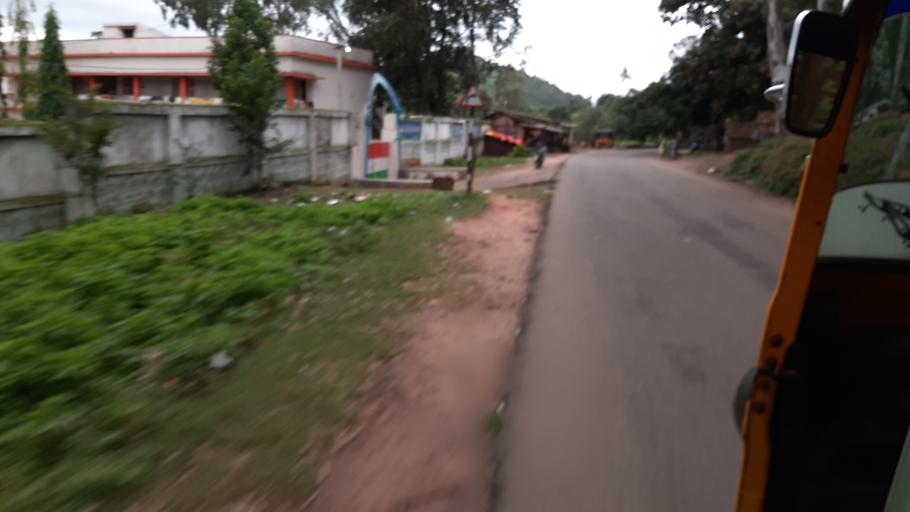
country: IN
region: Andhra Pradesh
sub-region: Vizianagaram District
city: Salur
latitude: 18.2363
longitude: 83.0050
